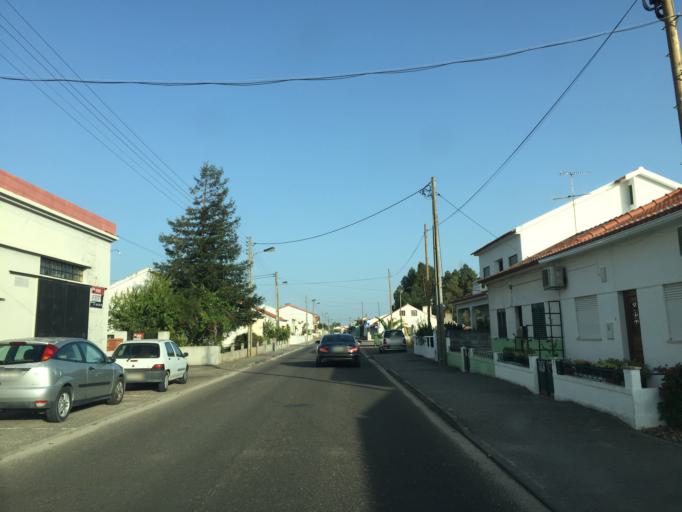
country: PT
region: Santarem
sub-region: Entroncamento
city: Entroncamento
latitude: 39.4731
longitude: -8.4465
